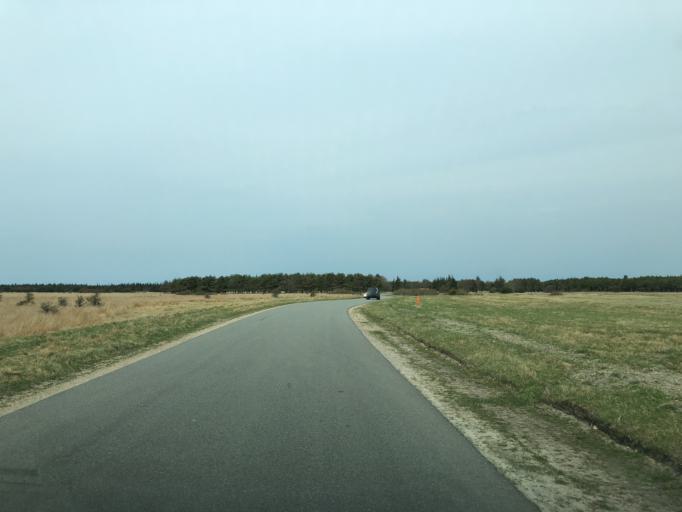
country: DK
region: South Denmark
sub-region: Varde Kommune
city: Oksbol
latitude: 55.6213
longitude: 8.1692
